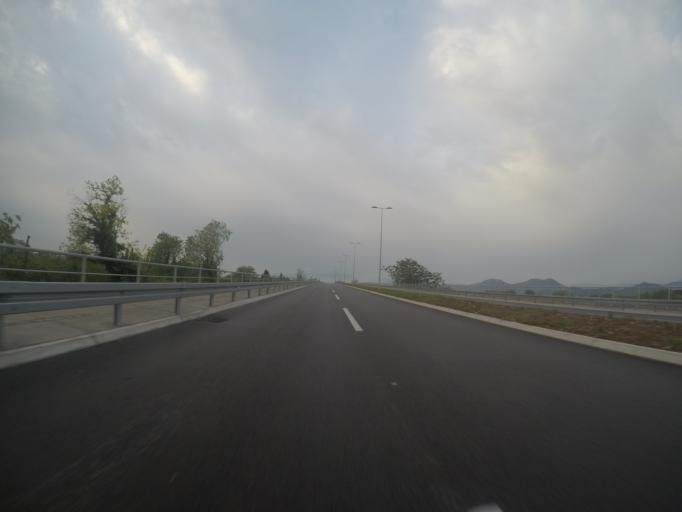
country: ME
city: Mojanovici
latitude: 42.3501
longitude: 19.2224
